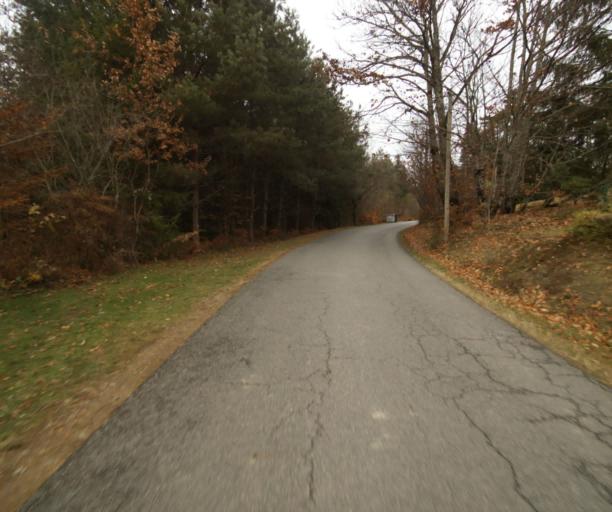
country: FR
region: Limousin
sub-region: Departement de la Correze
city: Saint-Mexant
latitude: 45.2644
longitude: 1.6646
